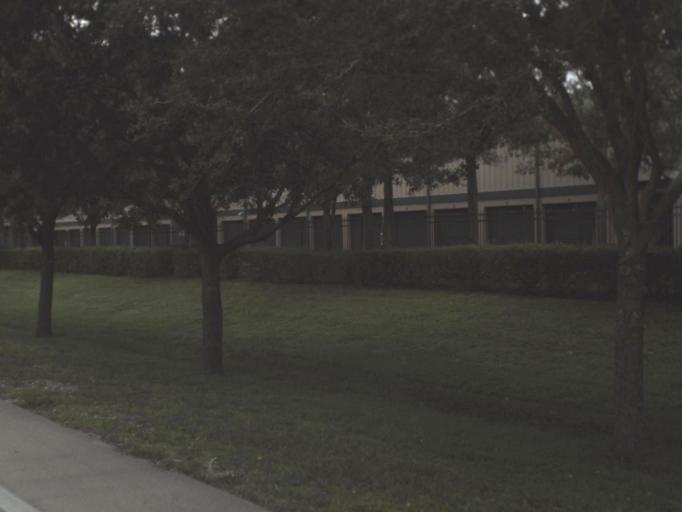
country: US
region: Florida
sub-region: Lee County
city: Fort Myers Shores
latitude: 26.7045
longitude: -81.7478
